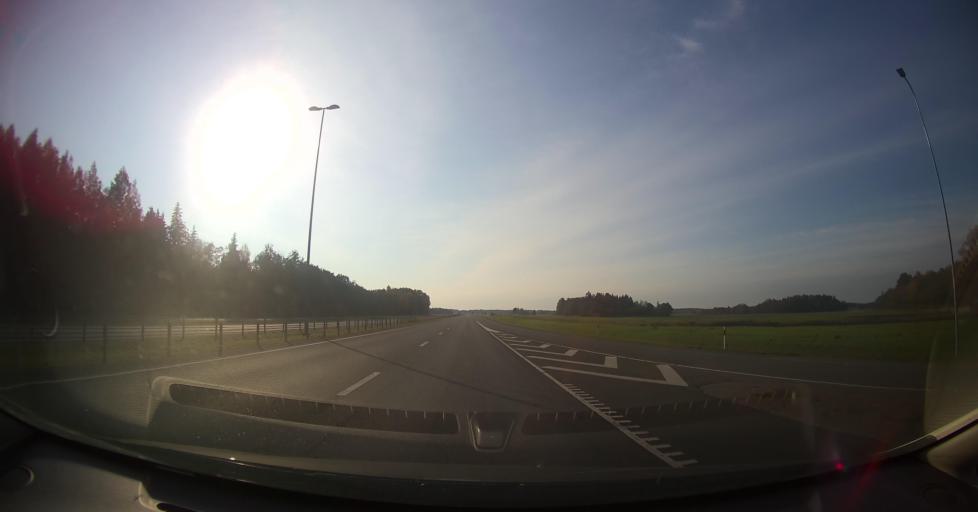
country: EE
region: Harju
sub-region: Rae vald
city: Vaida
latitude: 59.2164
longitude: 25.0371
